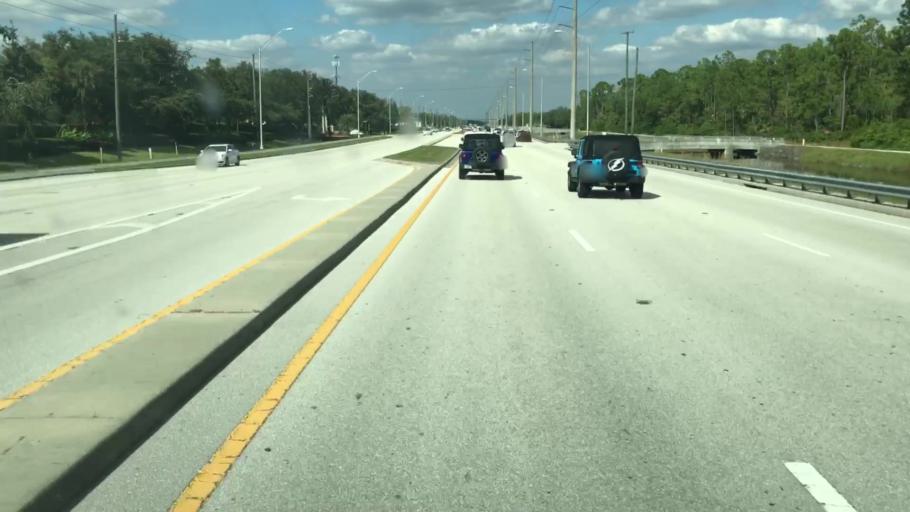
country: US
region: Florida
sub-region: Collier County
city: Vineyards
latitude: 26.2529
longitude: -81.6885
